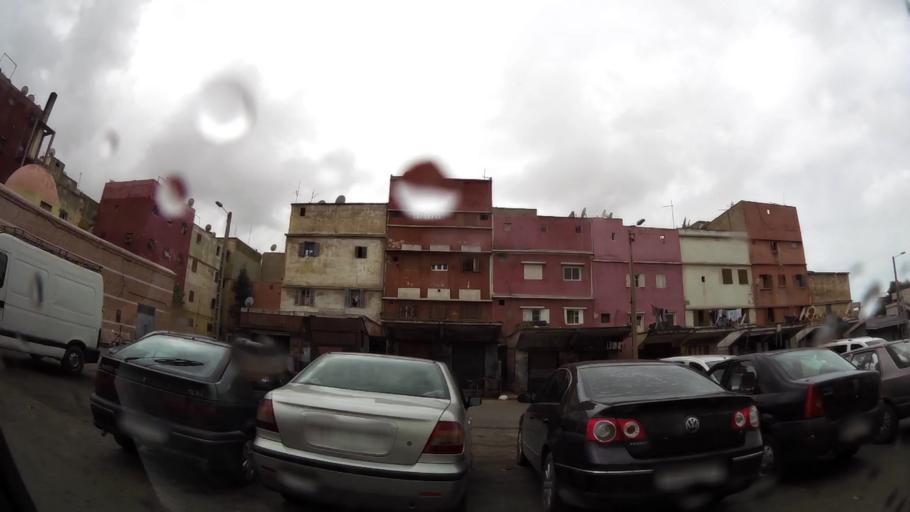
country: MA
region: Grand Casablanca
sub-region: Mediouna
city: Tit Mellil
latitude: 33.6074
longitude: -7.5076
